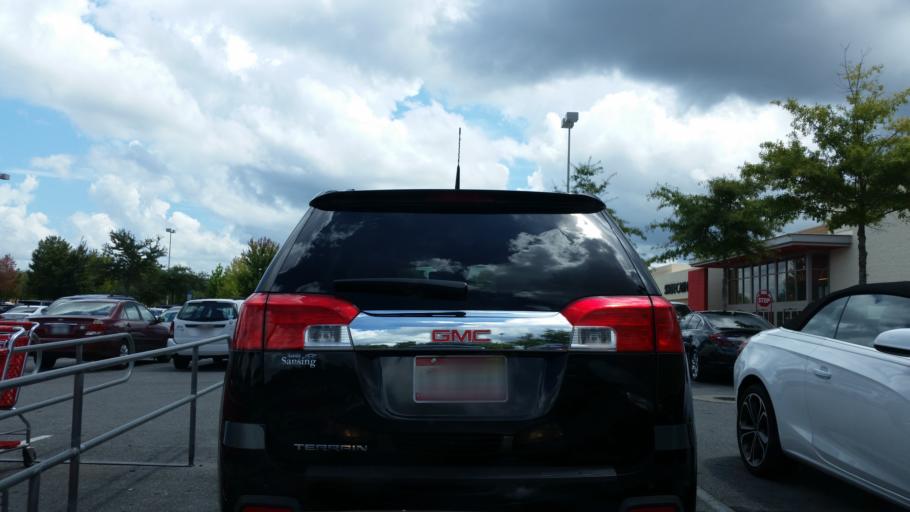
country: US
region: Florida
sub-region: Santa Rosa County
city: Pace
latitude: 30.6014
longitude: -87.1269
